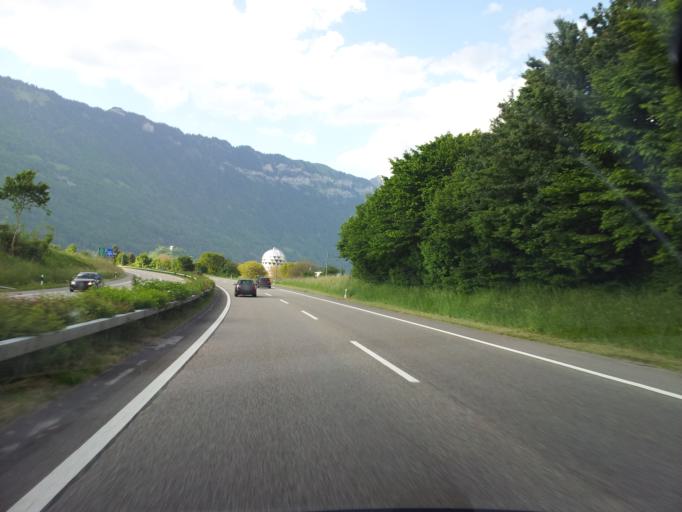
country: CH
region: Bern
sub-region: Interlaken-Oberhasli District
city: Matten
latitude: 46.6768
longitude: 7.8754
